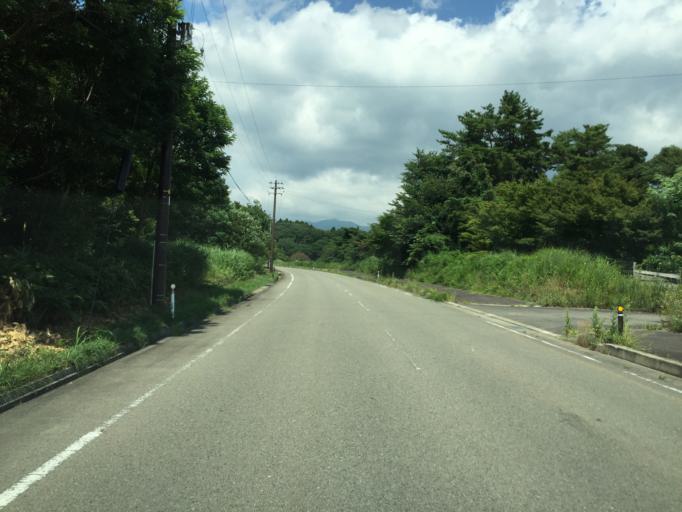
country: JP
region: Fukushima
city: Inawashiro
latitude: 37.5123
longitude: 140.0196
